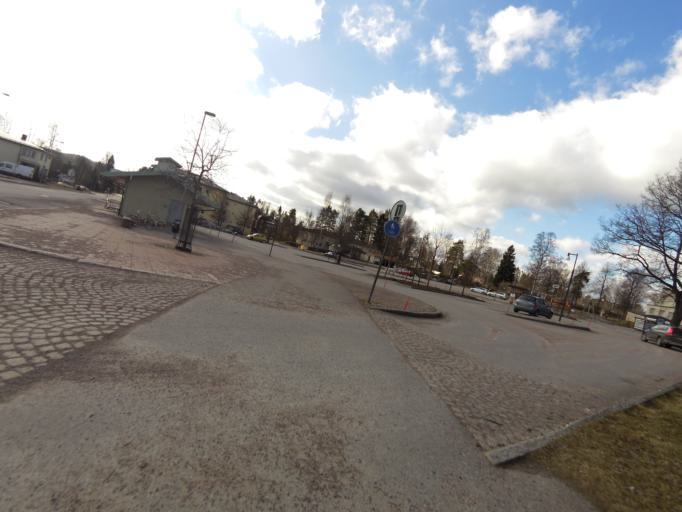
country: SE
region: Gaevleborg
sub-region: Hofors Kommun
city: Hofors
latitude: 60.5454
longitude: 16.2865
